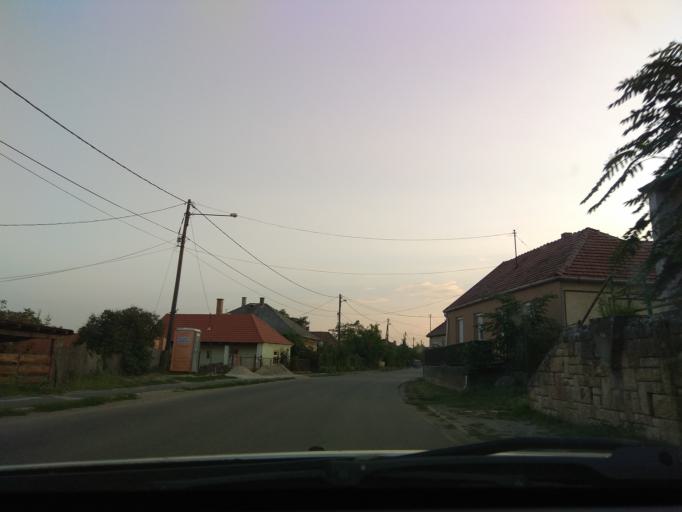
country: HU
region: Borsod-Abauj-Zemplen
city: Szerencs
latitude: 48.1891
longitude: 21.2143
